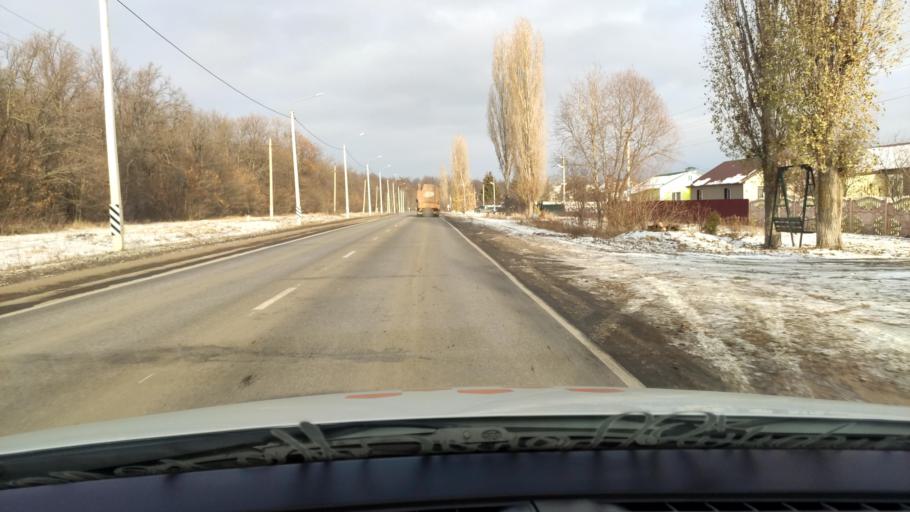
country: RU
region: Voronezj
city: Semiluki
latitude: 51.7355
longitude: 39.0428
